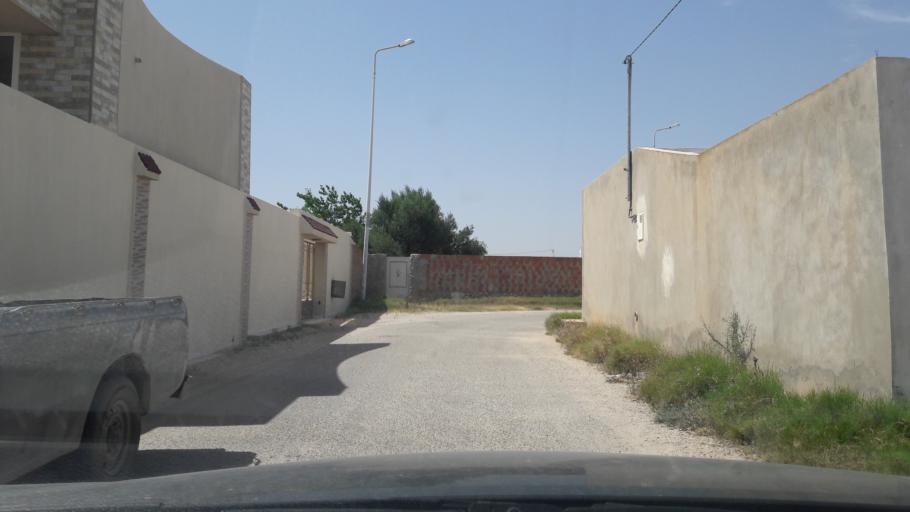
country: TN
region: Safaqis
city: Al Qarmadah
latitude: 34.7778
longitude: 10.7689
